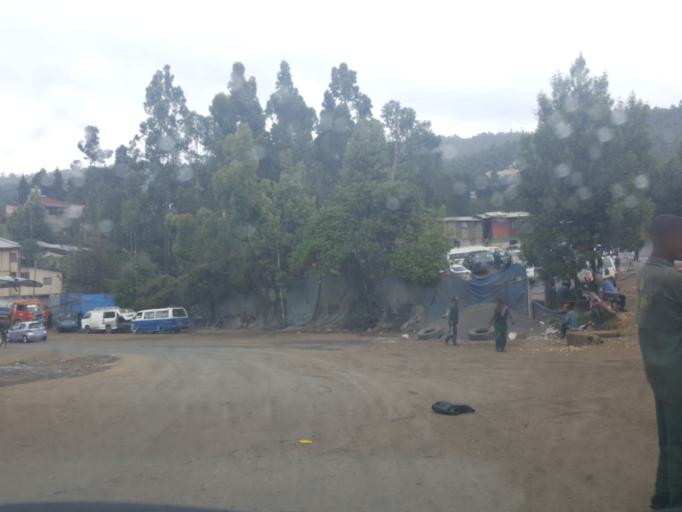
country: ET
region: Adis Abeba
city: Addis Ababa
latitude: 9.0698
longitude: 38.7390
